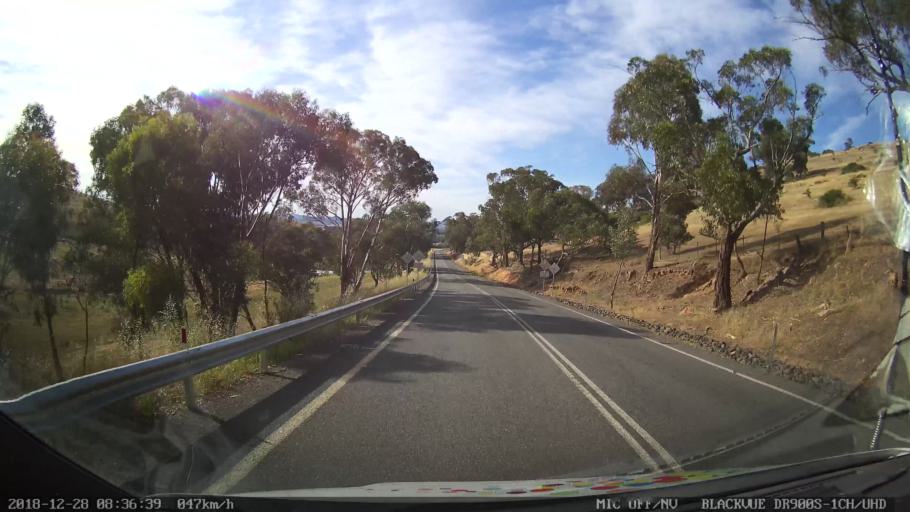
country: AU
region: New South Wales
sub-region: Blayney
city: Blayney
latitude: -33.9888
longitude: 149.3121
